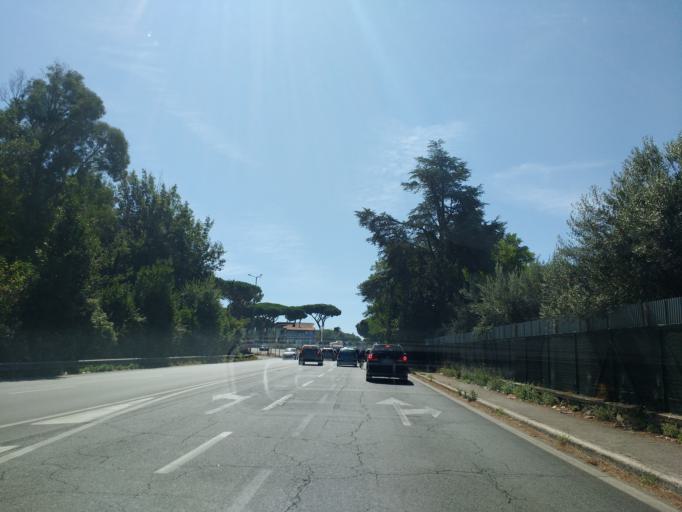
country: IT
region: Latium
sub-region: Citta metropolitana di Roma Capitale
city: Marino
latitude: 41.7563
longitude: 12.6279
